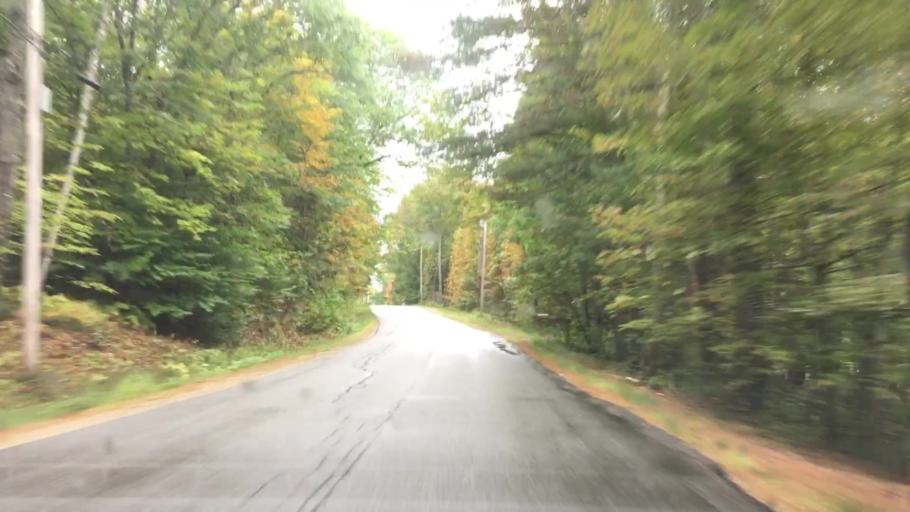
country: US
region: Maine
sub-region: Cumberland County
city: Harrison
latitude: 44.0613
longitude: -70.6250
